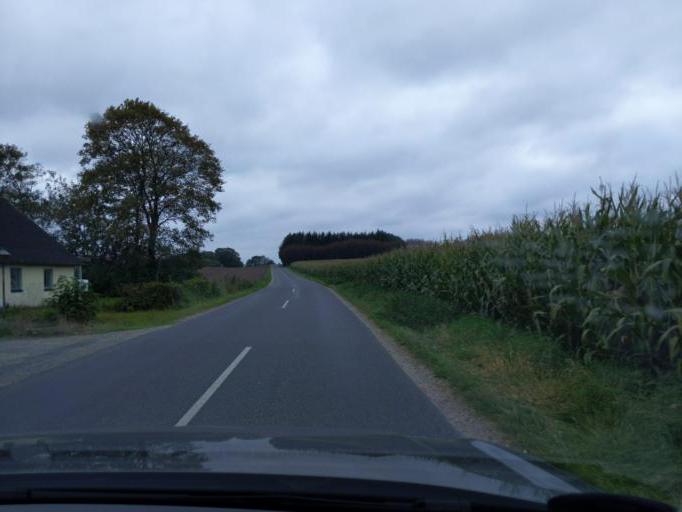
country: DK
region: North Denmark
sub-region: Mariagerfjord Kommune
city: Hobro
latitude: 56.5569
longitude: 9.6700
